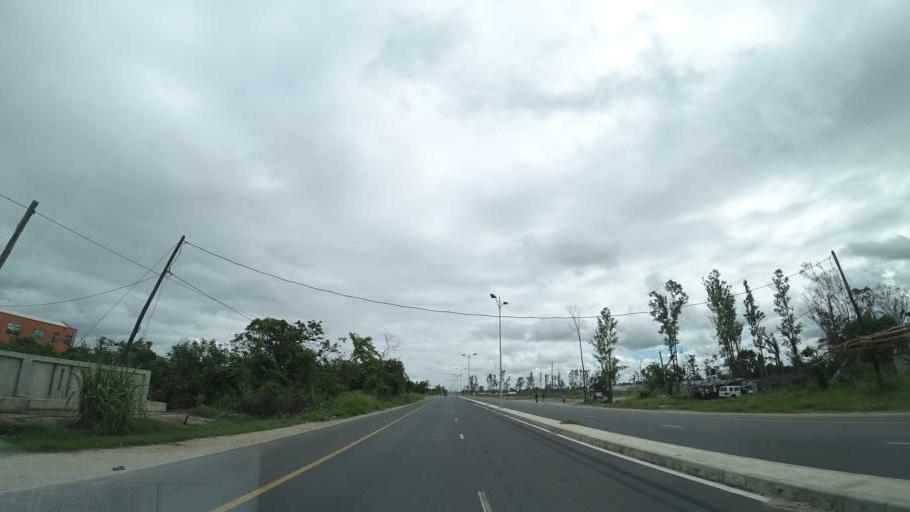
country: MZ
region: Sofala
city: Dondo
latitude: -19.7046
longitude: 34.7902
